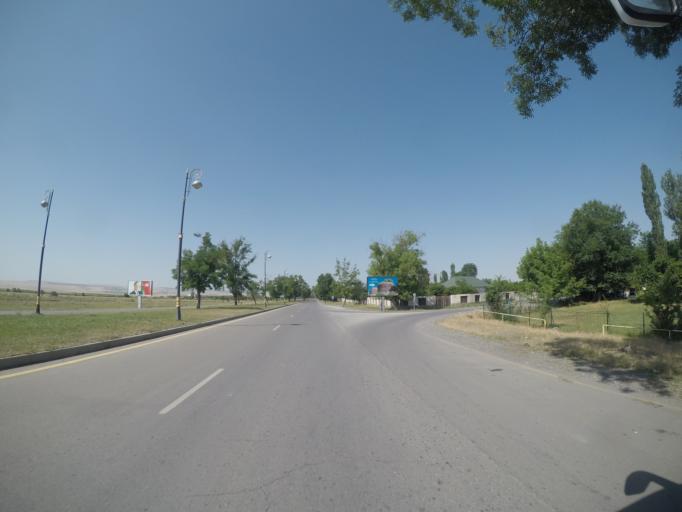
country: AZ
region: Goeycay
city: Geoktschai
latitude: 40.8366
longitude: 47.7172
